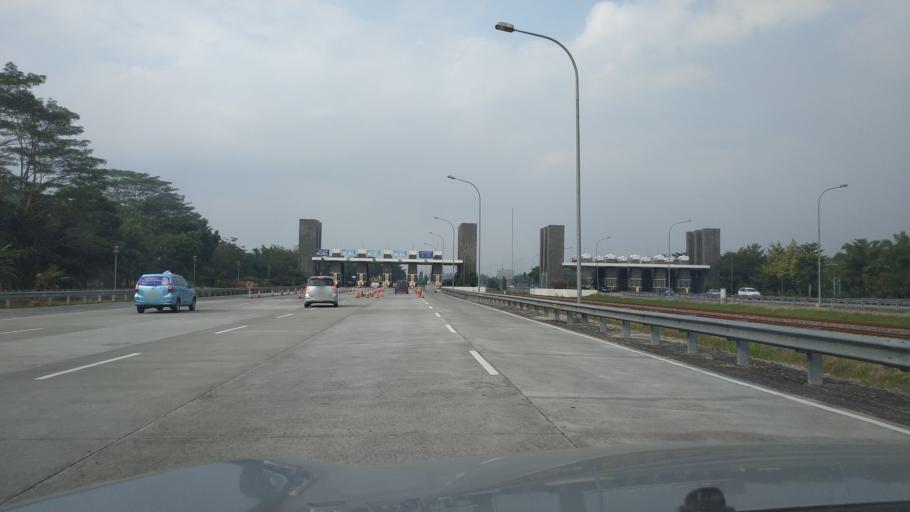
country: ID
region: North Sumatra
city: Percut
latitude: 3.6147
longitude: 98.8586
